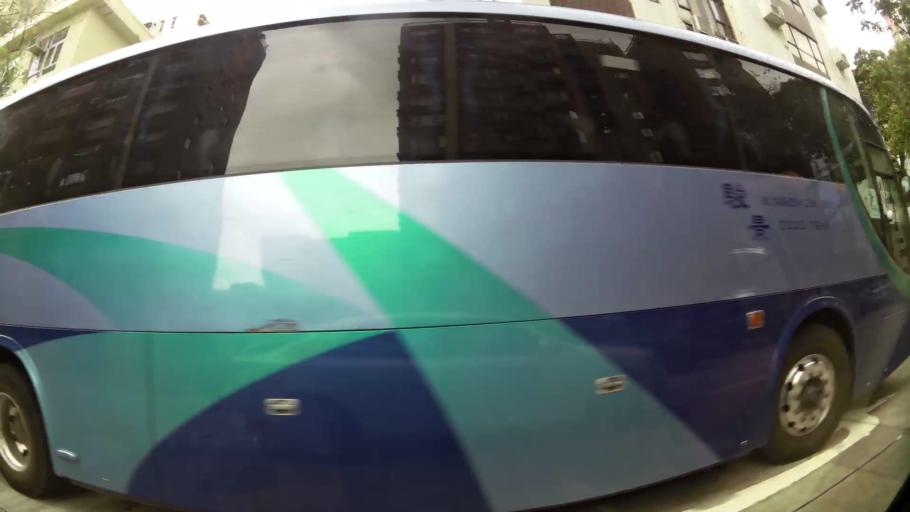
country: HK
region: Kowloon City
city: Kowloon
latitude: 22.3265
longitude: 114.1804
